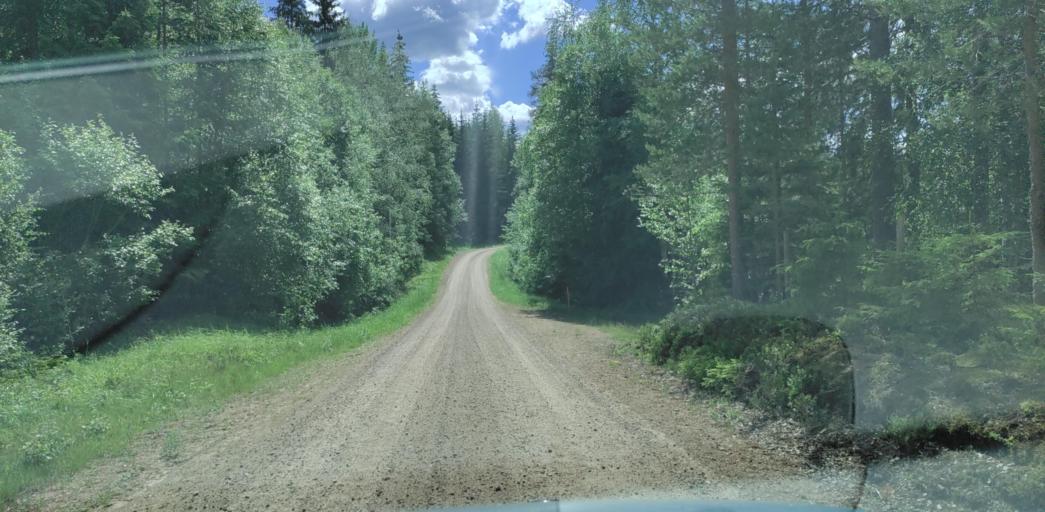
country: SE
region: Vaermland
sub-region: Hagfors Kommun
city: Ekshaerad
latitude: 60.0919
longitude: 13.3149
